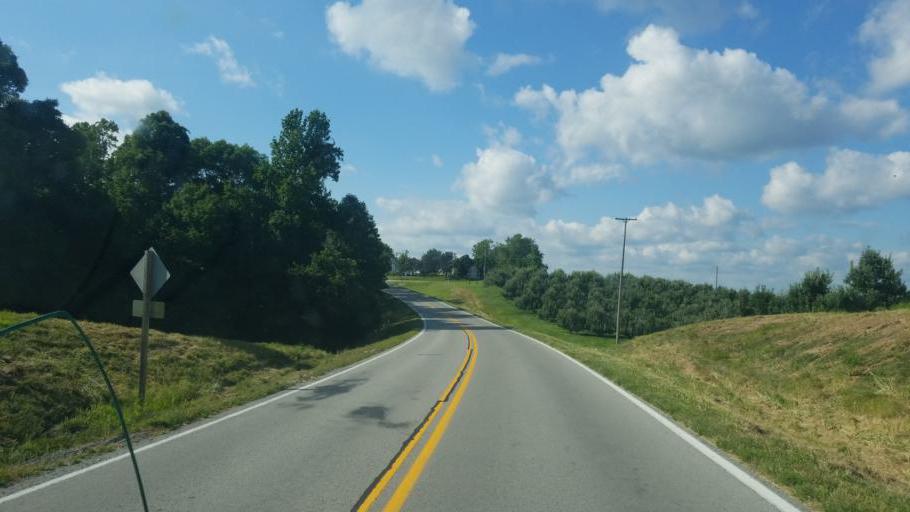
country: US
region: Illinois
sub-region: Union County
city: Cobden
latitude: 37.5977
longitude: -89.3215
